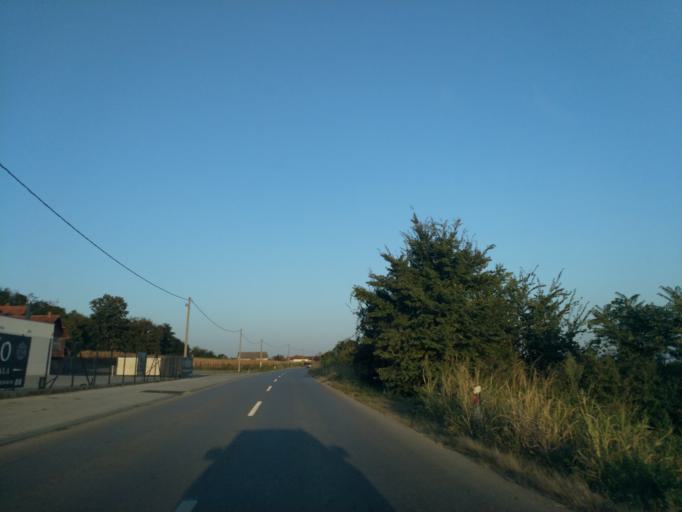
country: RS
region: Central Serbia
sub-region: Rasinski Okrug
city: Trstenik
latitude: 43.6293
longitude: 21.0488
